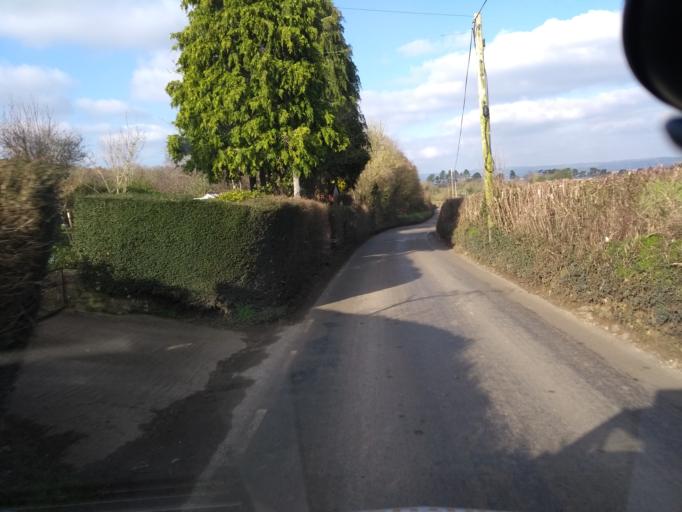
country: GB
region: England
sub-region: Somerset
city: Creech Saint Michael
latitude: 50.9731
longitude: -3.0539
